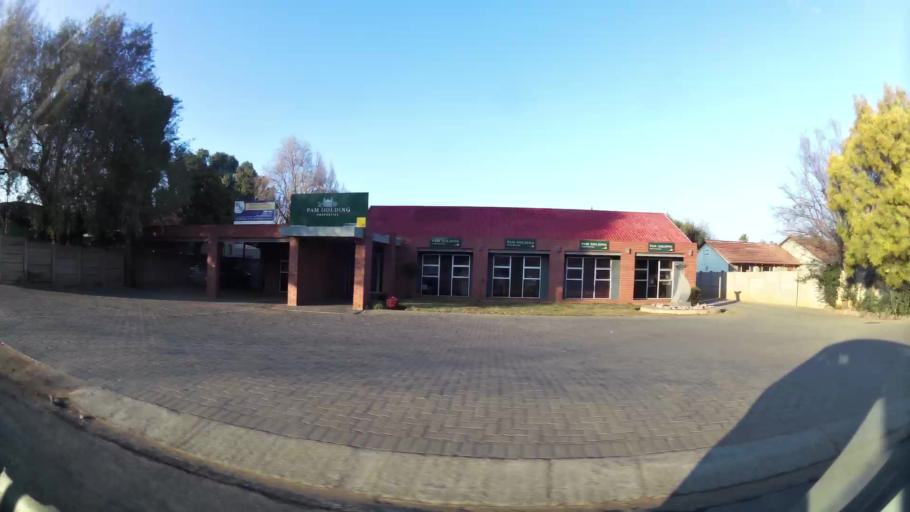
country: ZA
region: Orange Free State
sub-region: Mangaung Metropolitan Municipality
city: Bloemfontein
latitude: -29.1013
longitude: 26.1574
